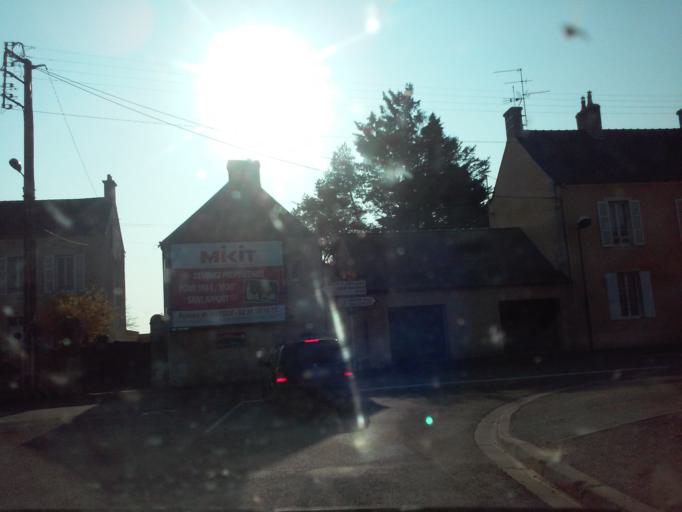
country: FR
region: Lower Normandy
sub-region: Departement du Calvados
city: Bayeux
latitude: 49.2670
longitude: -0.6955
